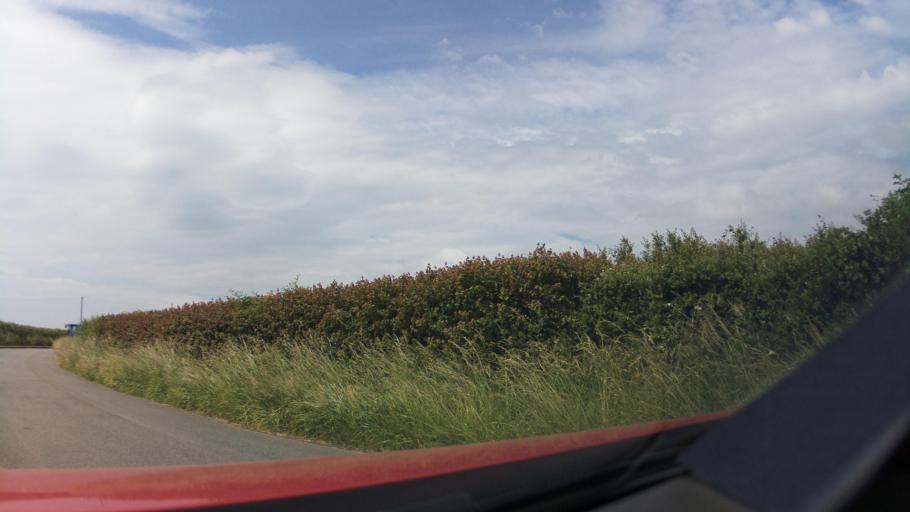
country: GB
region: Wales
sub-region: Vale of Glamorgan
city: Wick
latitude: 51.4090
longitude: -3.5382
